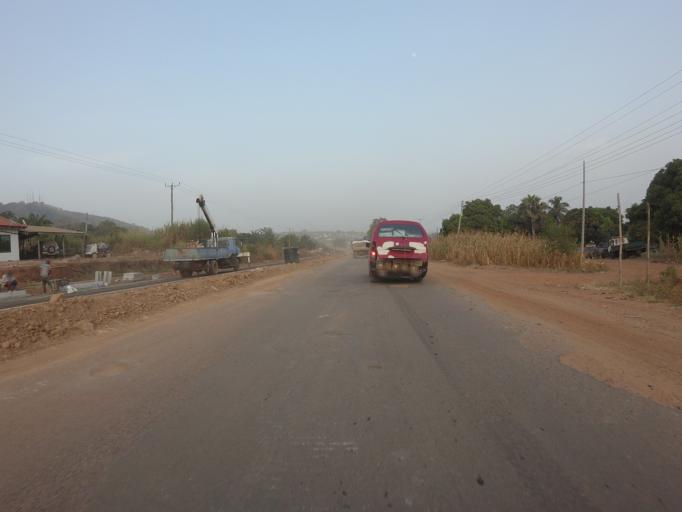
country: GH
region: Volta
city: Ho
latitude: 6.5935
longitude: 0.4372
